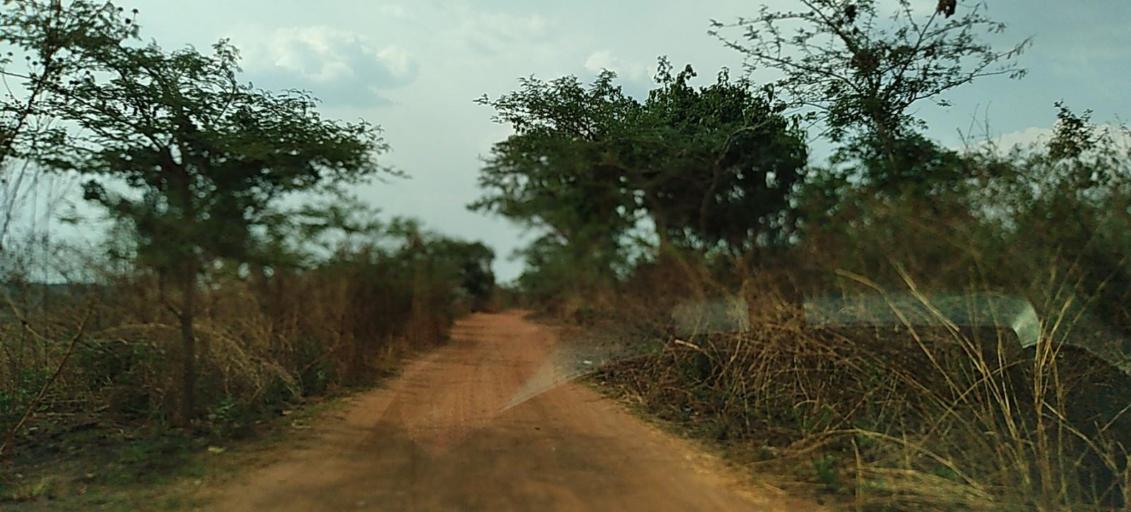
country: ZM
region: Copperbelt
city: Chililabombwe
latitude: -12.3952
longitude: 27.8039
